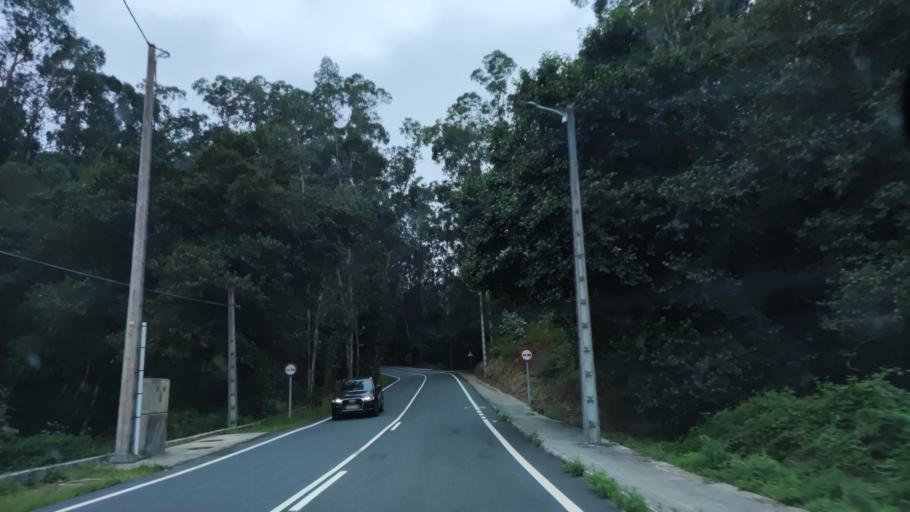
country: ES
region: Galicia
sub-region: Provincia de Pontevedra
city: Catoira
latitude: 42.6846
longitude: -8.7338
